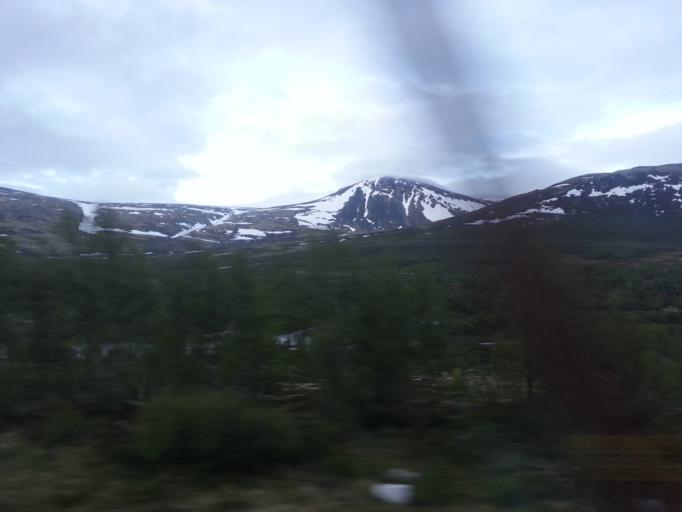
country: NO
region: Oppland
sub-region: Dovre
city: Dovre
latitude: 62.1753
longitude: 9.4408
